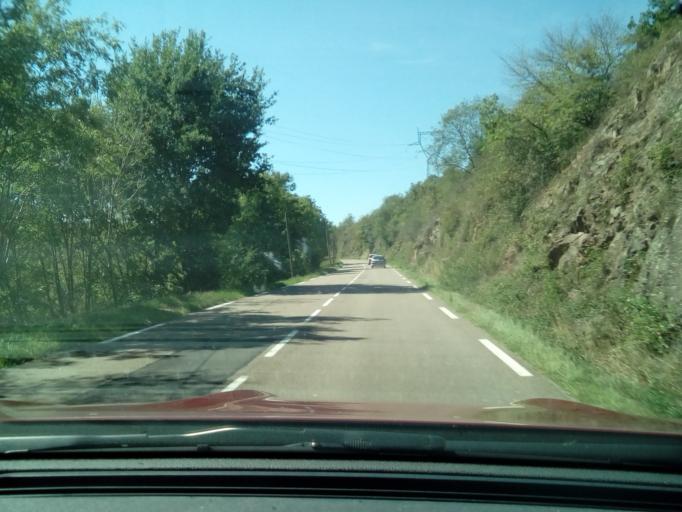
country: FR
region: Rhone-Alpes
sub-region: Departement du Rhone
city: Saint-Verand
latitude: 45.9035
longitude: 4.5330
